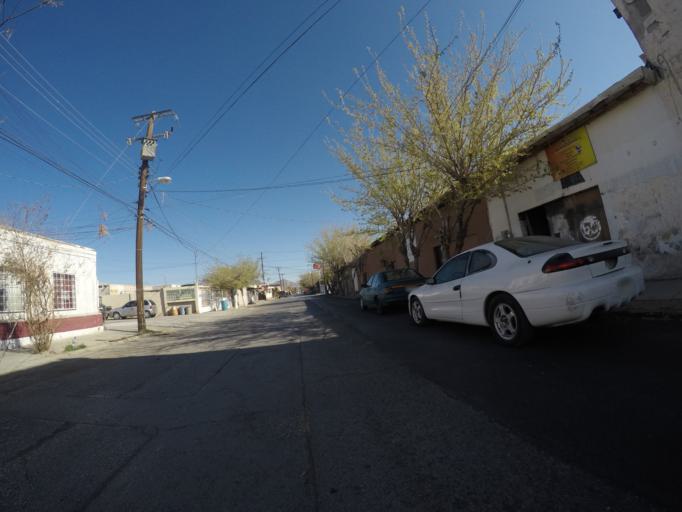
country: MX
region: Chihuahua
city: Ciudad Juarez
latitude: 31.7433
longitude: -106.4718
